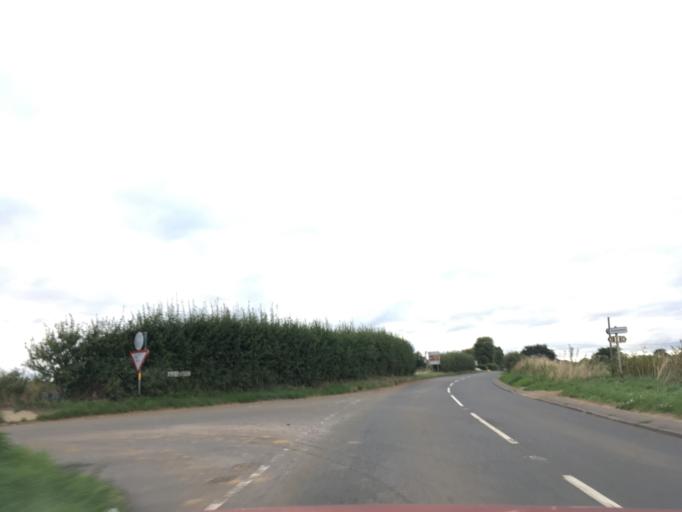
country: GB
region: England
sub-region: Wiltshire
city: Devizes
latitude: 51.3847
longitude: -2.0394
